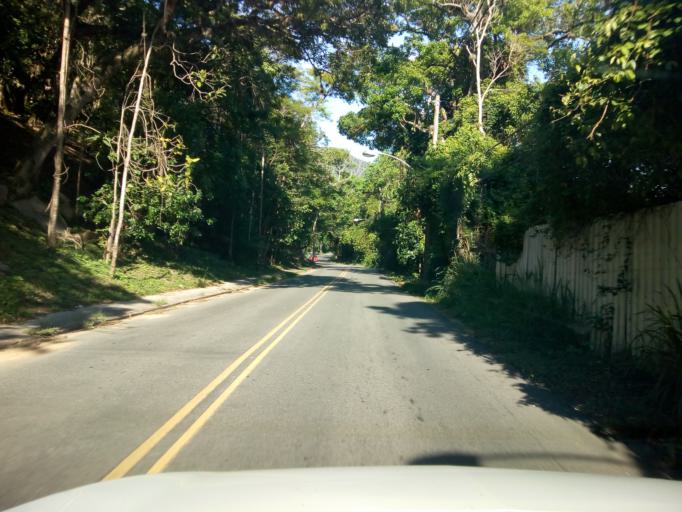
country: BR
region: Rio de Janeiro
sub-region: Nilopolis
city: Nilopolis
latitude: -23.0256
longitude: -43.5061
